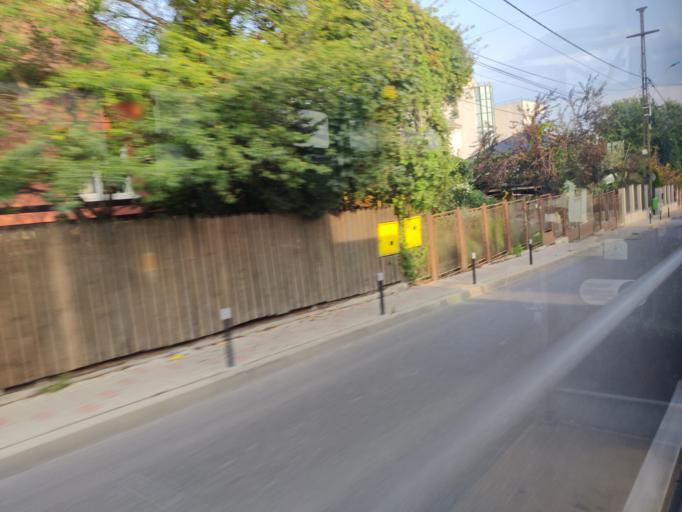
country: RO
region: Iasi
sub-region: Municipiul Iasi
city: Iasi
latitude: 47.1715
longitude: 27.5995
